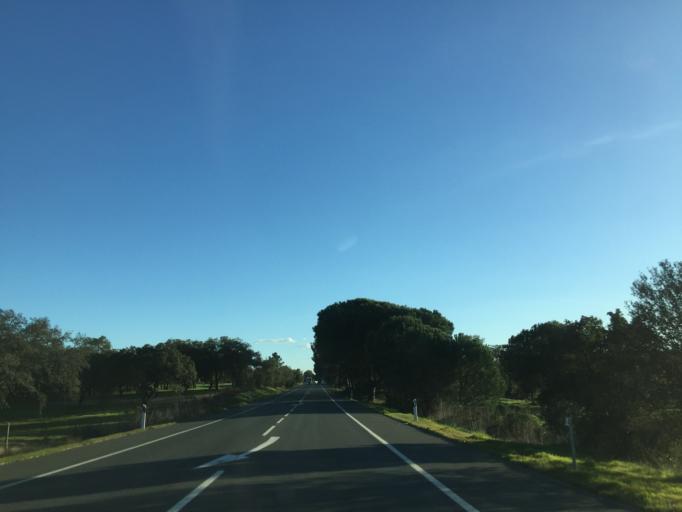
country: PT
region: Setubal
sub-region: Grandola
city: Grandola
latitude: 38.0495
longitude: -8.4021
